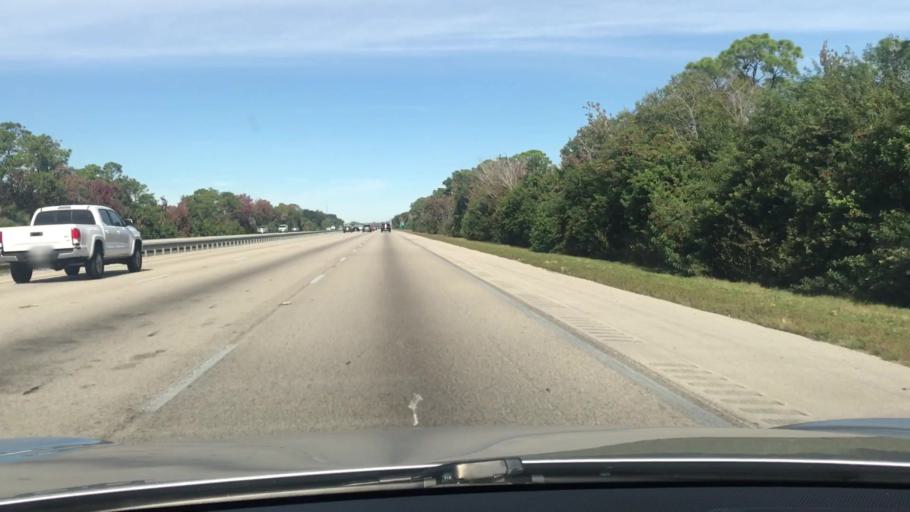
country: US
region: Florida
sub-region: Brevard County
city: South Patrick Shores
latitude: 28.1710
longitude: -80.7056
